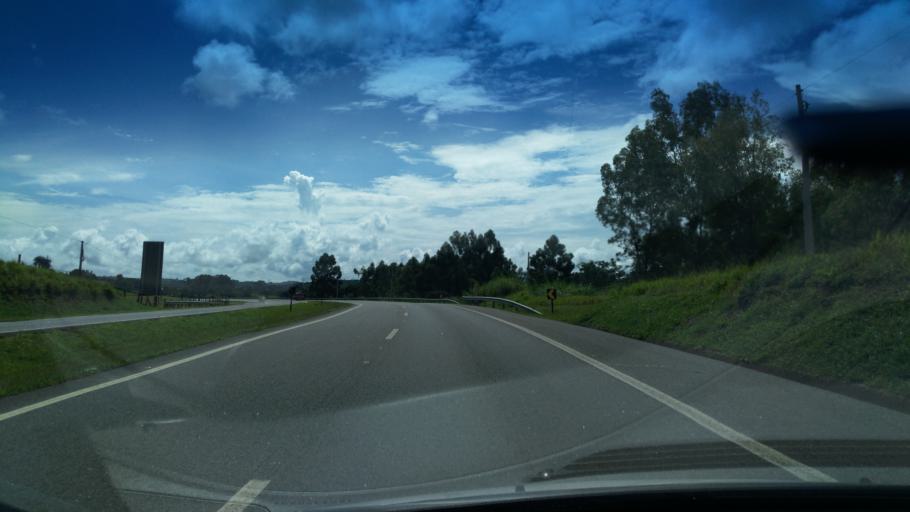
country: BR
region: Sao Paulo
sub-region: Santo Antonio Do Jardim
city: Espirito Santo do Pinhal
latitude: -22.2070
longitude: -46.7786
